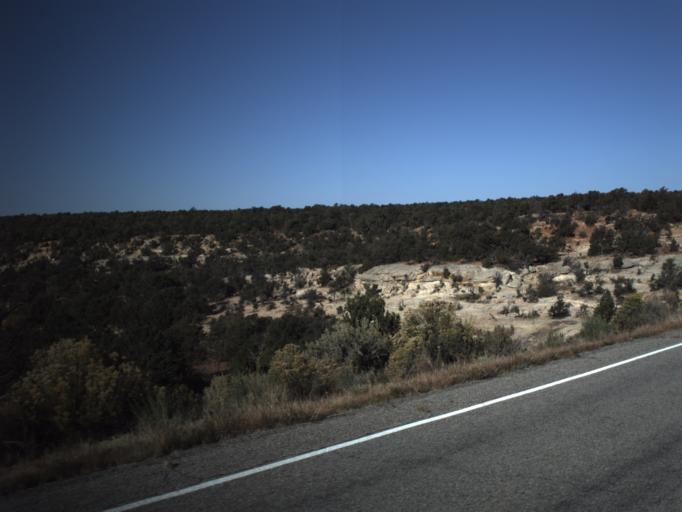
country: US
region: Utah
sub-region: San Juan County
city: Blanding
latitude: 37.5834
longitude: -109.8918
